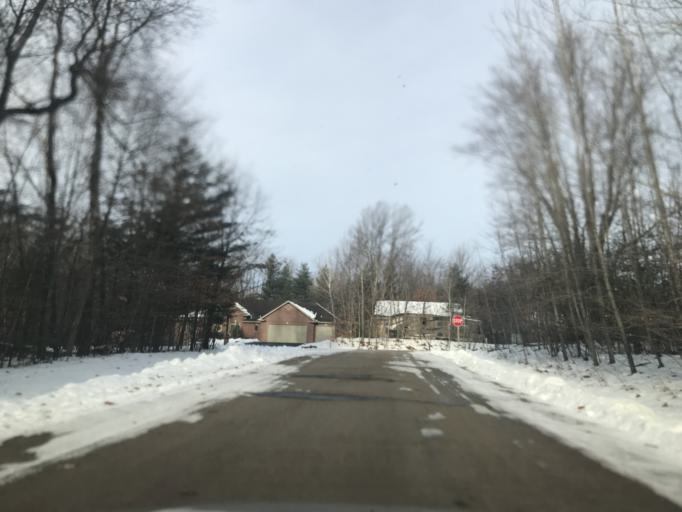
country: US
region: Wisconsin
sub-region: Brown County
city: Suamico
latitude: 44.6860
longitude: -88.0570
